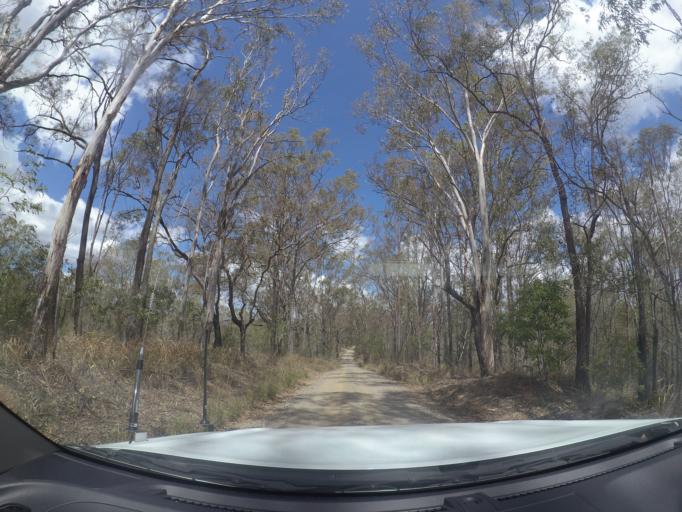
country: AU
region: Queensland
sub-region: Logan
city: Cedar Vale
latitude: -27.8985
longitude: 153.0445
